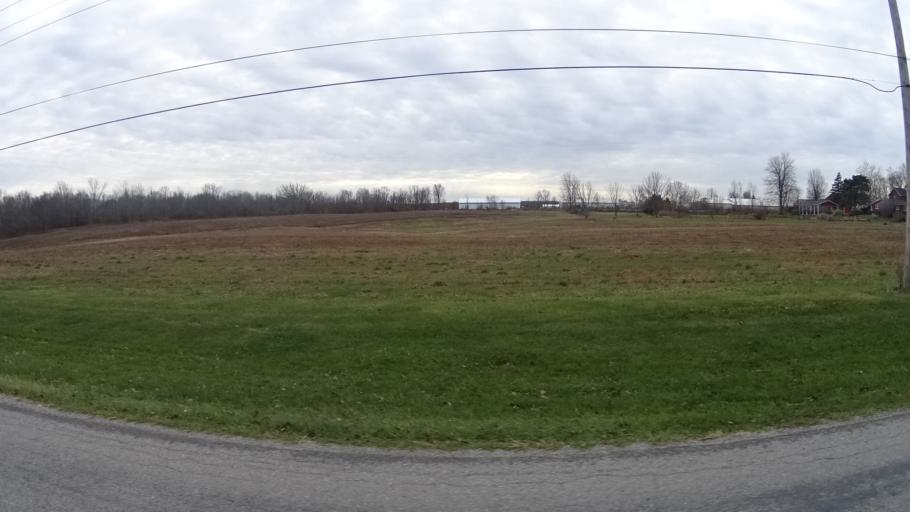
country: US
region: Ohio
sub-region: Lorain County
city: Wellington
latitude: 41.1581
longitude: -82.2145
